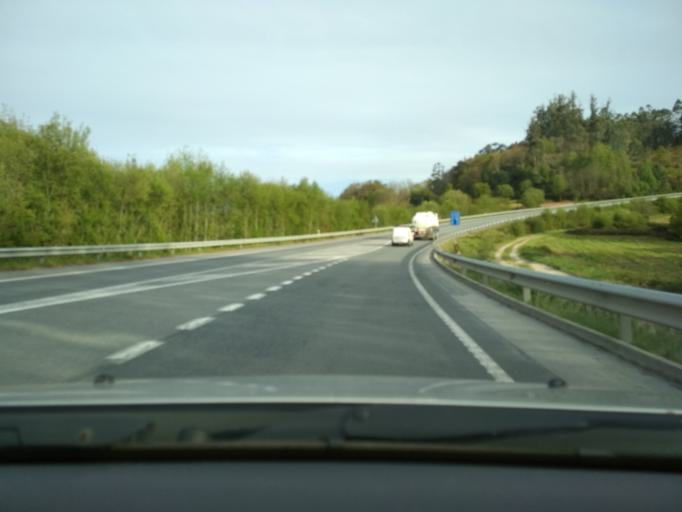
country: ES
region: Galicia
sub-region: Provincia da Coruna
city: Cerceda
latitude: 43.2180
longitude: -8.4563
